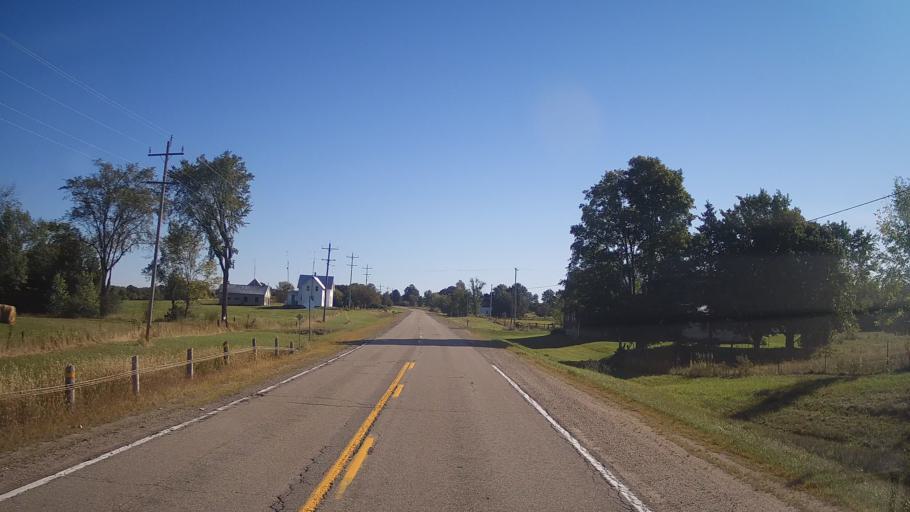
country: CA
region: Ontario
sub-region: Lanark County
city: Smiths Falls
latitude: 44.6115
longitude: -76.0573
